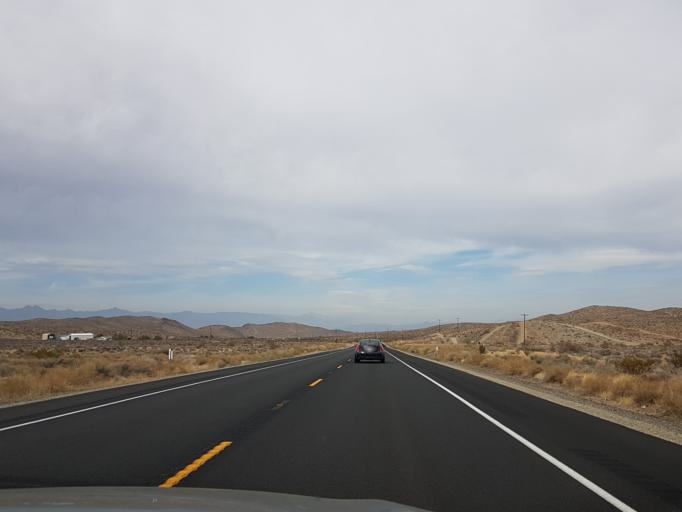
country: US
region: California
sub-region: Kern County
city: Ridgecrest
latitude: 35.5171
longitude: -117.6718
